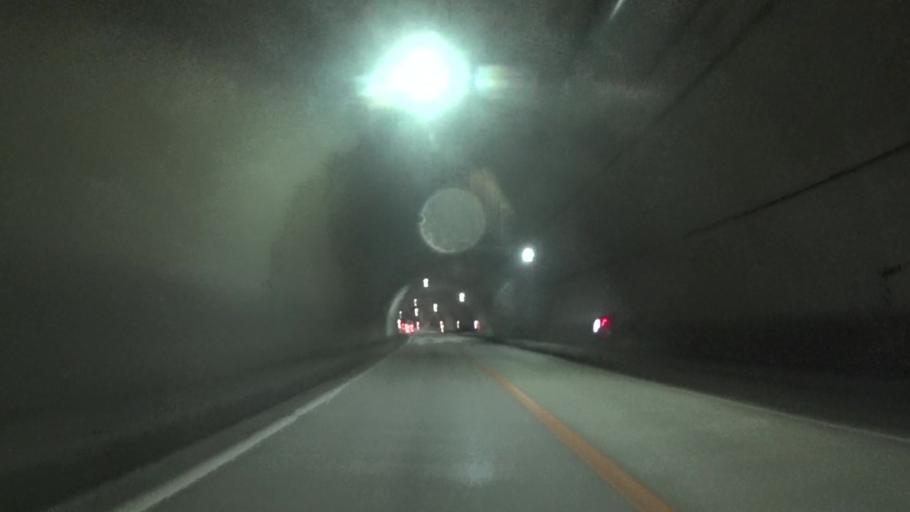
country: JP
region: Kyoto
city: Kameoka
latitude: 35.1295
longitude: 135.6462
